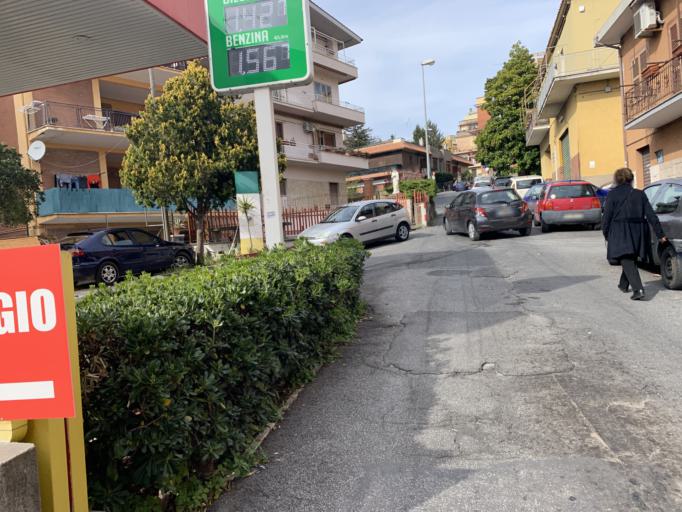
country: IT
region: Latium
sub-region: Citta metropolitana di Roma Capitale
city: Grottaferrata
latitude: 41.7688
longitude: 12.6660
